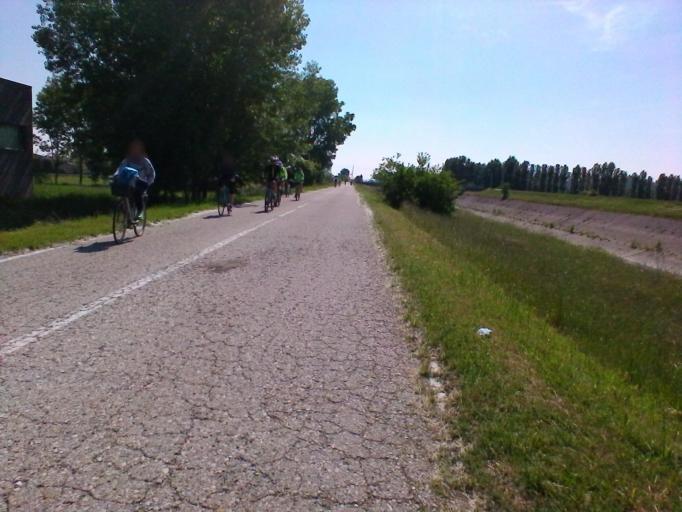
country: IT
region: Lombardy
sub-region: Provincia di Mantova
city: Soave
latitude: 45.1961
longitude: 10.7156
